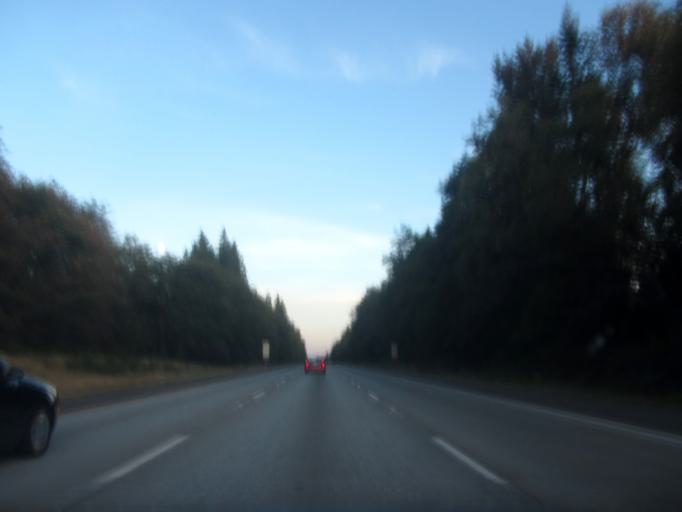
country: US
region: Washington
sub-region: Snohomish County
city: Bryant
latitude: 48.2593
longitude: -122.2617
